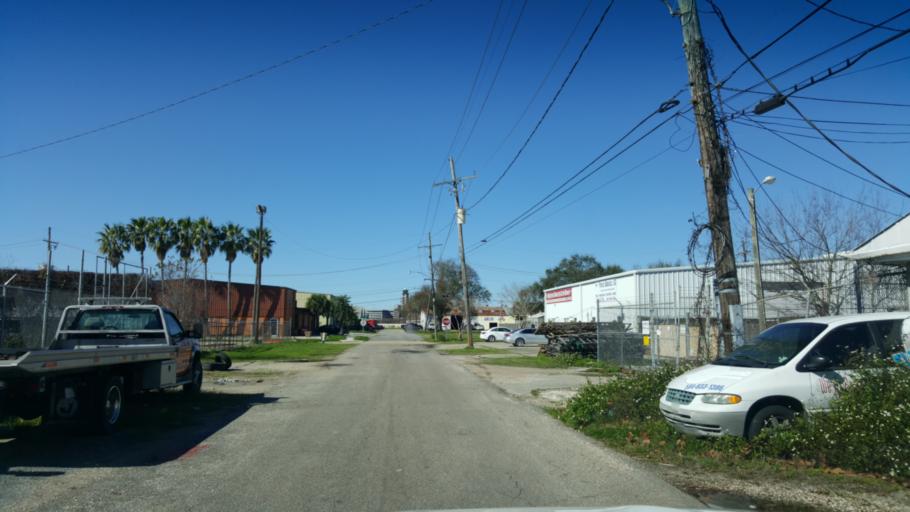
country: US
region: Louisiana
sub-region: Jefferson Parish
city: Kenner
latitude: 29.9813
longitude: -90.2470
